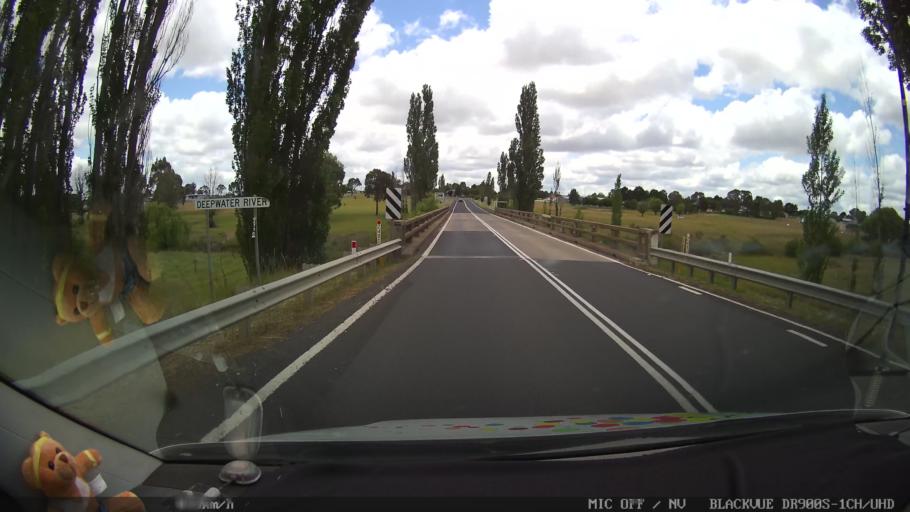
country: AU
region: New South Wales
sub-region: Glen Innes Severn
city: Glen Innes
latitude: -29.4462
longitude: 151.8431
